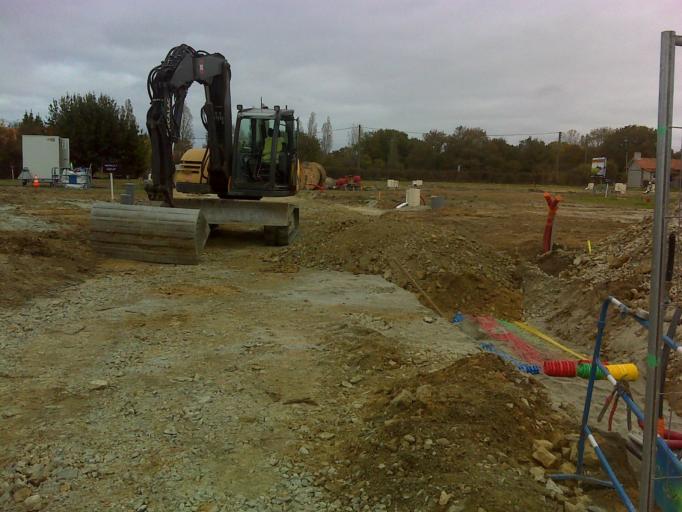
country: FR
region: Pays de la Loire
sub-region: Departement de la Loire-Atlantique
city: Pornic
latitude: 47.1027
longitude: -2.0644
